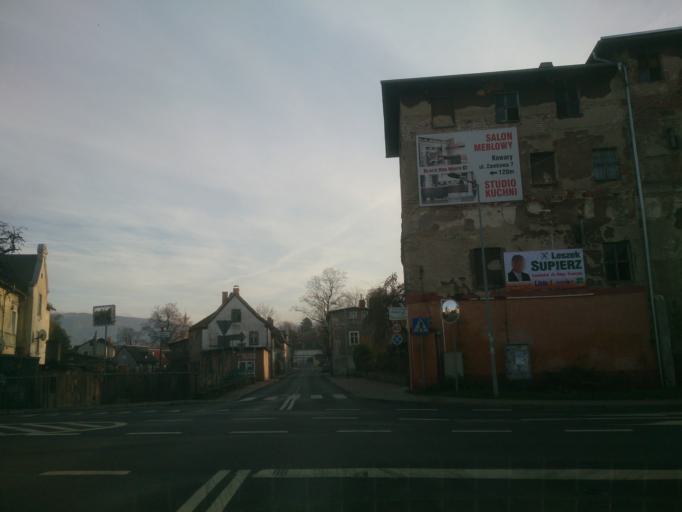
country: PL
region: Lower Silesian Voivodeship
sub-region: Powiat jeleniogorski
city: Kowary
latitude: 50.7996
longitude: 15.8275
